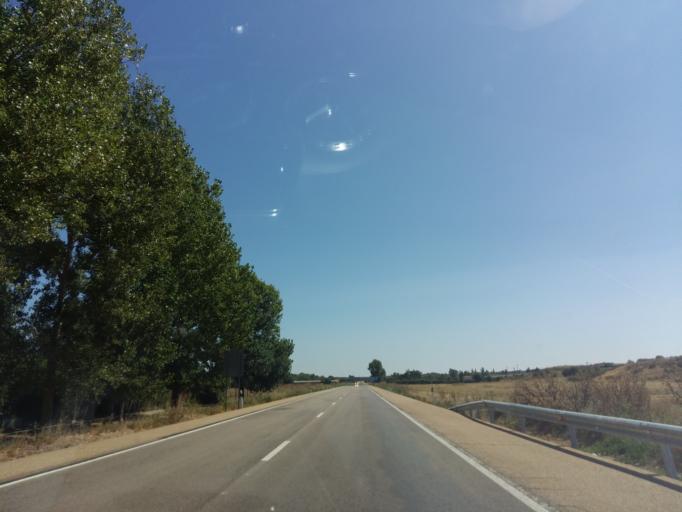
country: ES
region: Castille and Leon
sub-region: Provincia de Leon
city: Astorga
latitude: 42.4446
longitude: -6.0443
